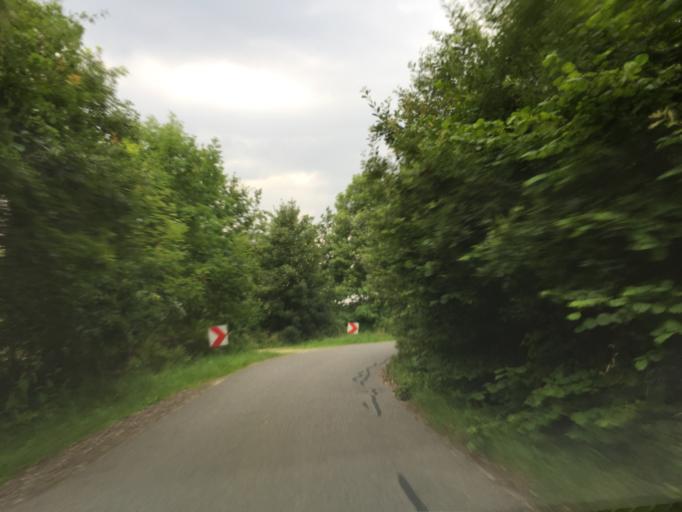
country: DK
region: Central Jutland
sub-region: Viborg Kommune
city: Bjerringbro
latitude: 56.3243
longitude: 9.6626
